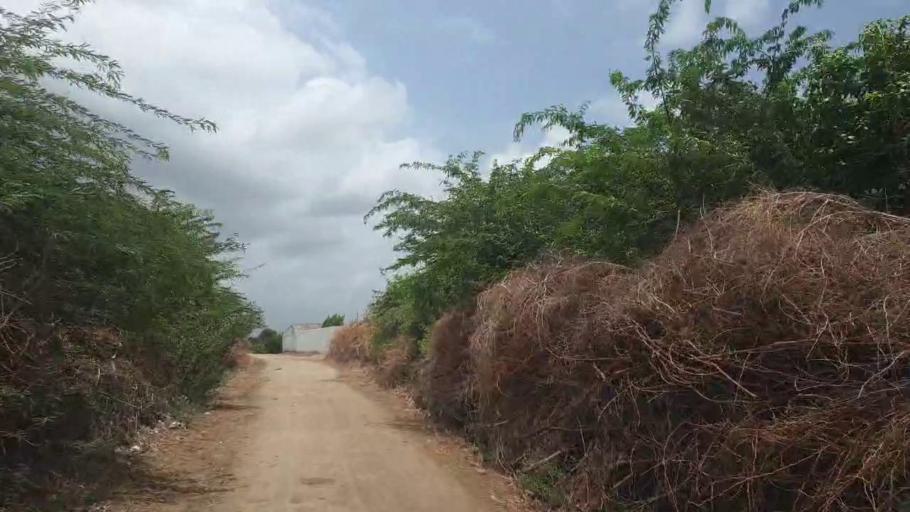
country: PK
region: Sindh
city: Badin
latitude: 24.6623
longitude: 68.9066
